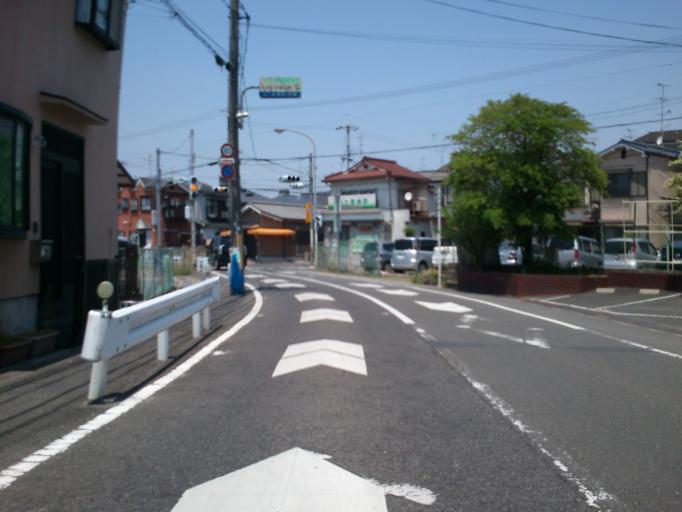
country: JP
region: Kyoto
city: Uji
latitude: 34.8663
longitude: 135.7706
